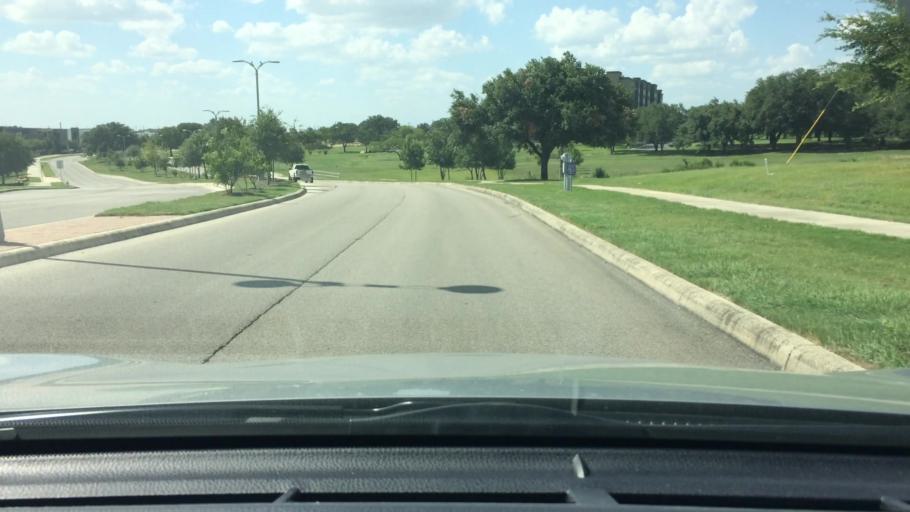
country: US
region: Texas
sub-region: Bexar County
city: San Antonio
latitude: 29.3465
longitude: -98.4452
